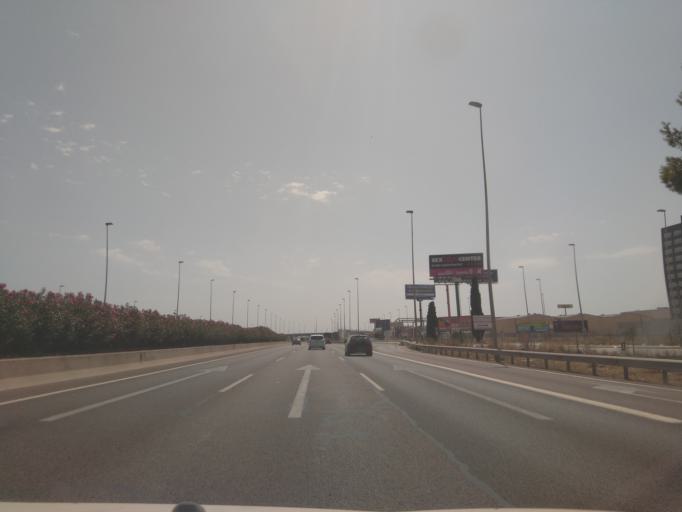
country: ES
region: Valencia
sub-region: Provincia de Valencia
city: Alfafar
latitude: 39.4155
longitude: -0.3778
